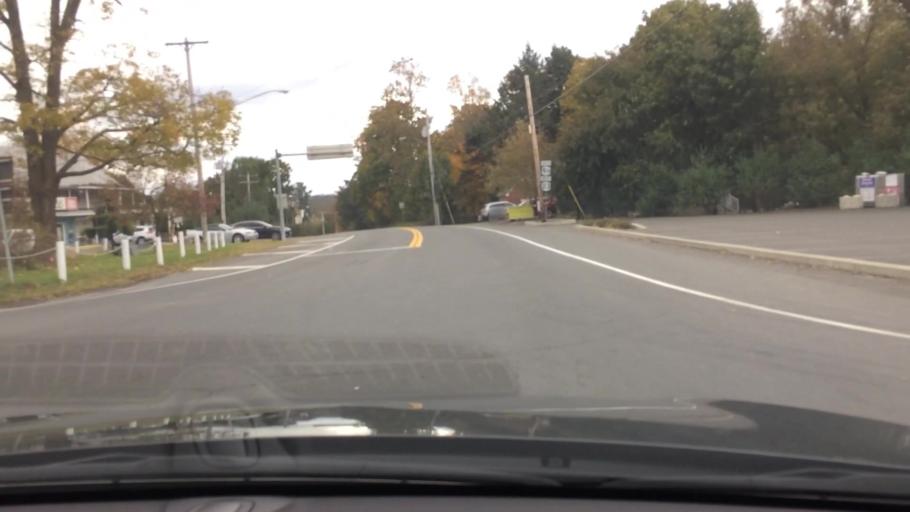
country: US
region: New York
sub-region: Columbia County
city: Lorenz Park
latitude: 42.2224
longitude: -73.7350
